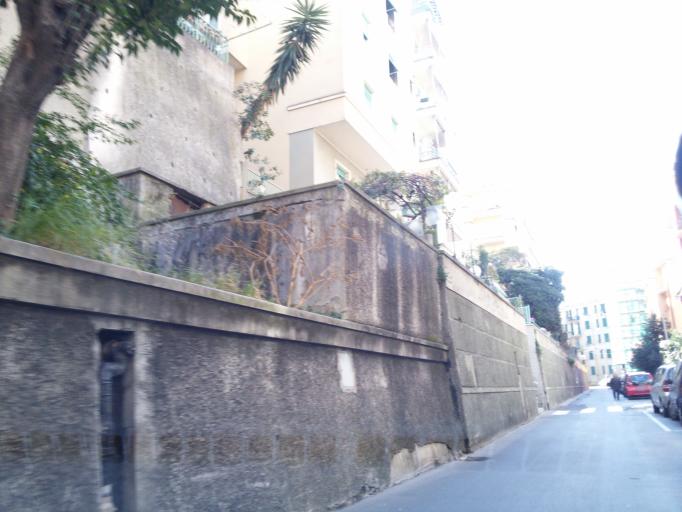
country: IT
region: Liguria
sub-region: Provincia di Genova
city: Genoa
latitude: 44.4114
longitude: 8.9595
